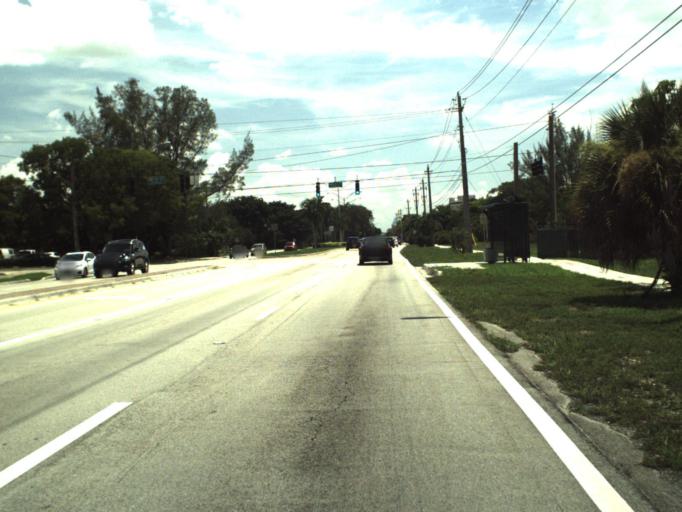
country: US
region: Florida
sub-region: Broward County
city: Coral Springs
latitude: 26.2803
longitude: -80.2504
